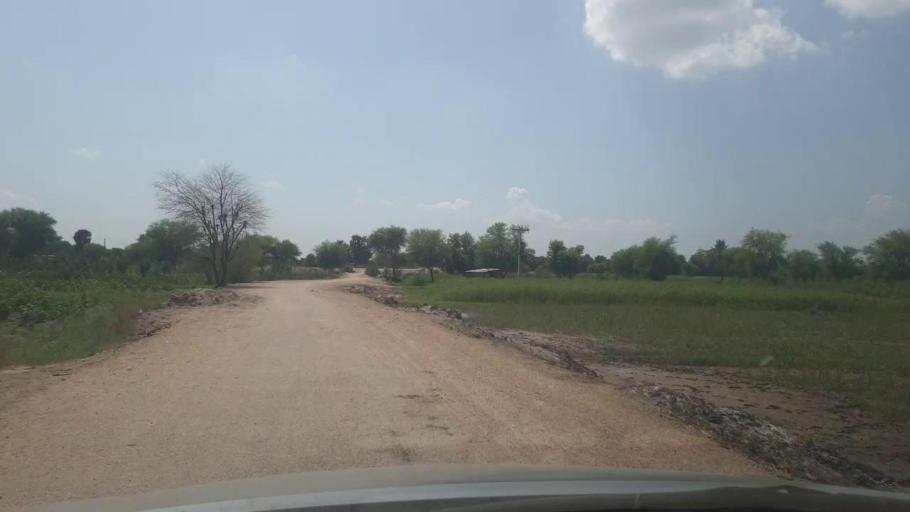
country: PK
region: Sindh
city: Khairpur
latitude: 27.5236
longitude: 68.7974
